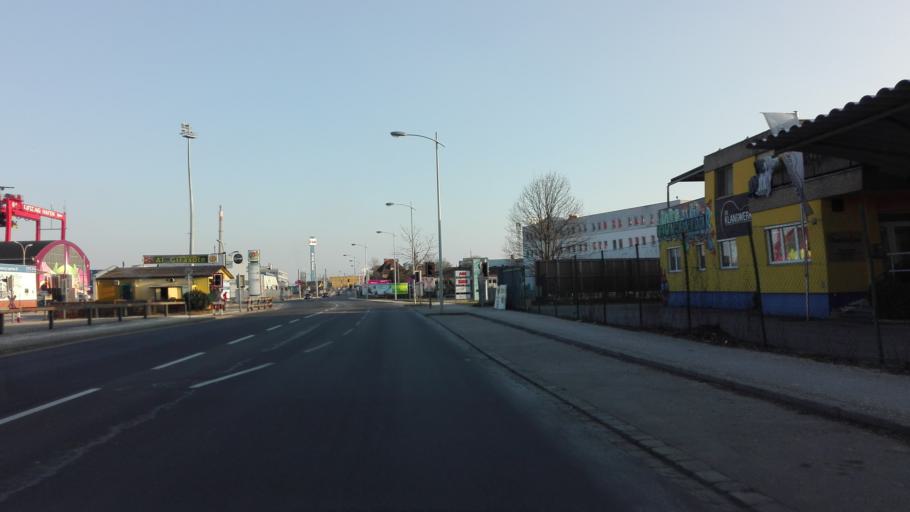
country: AT
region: Upper Austria
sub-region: Linz Stadt
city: Linz
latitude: 48.3123
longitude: 14.3131
